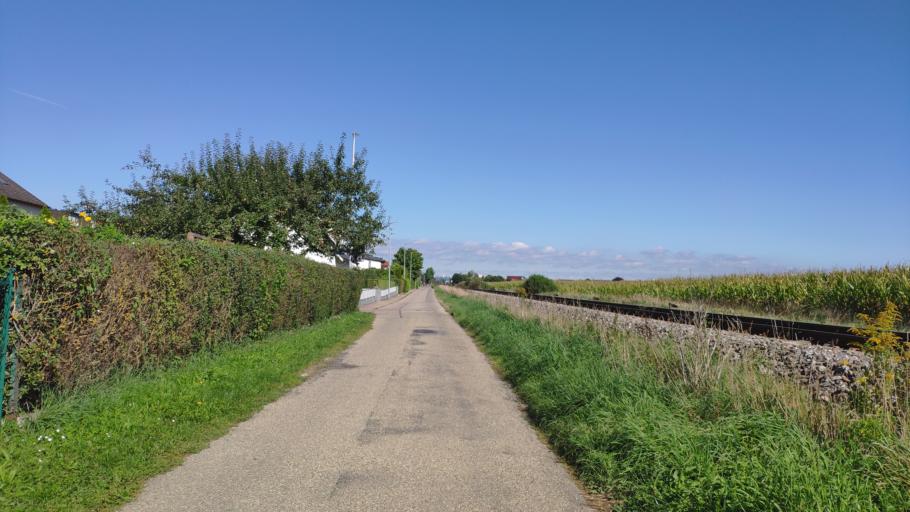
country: DE
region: Bavaria
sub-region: Swabia
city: Senden
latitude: 48.3445
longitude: 10.0391
